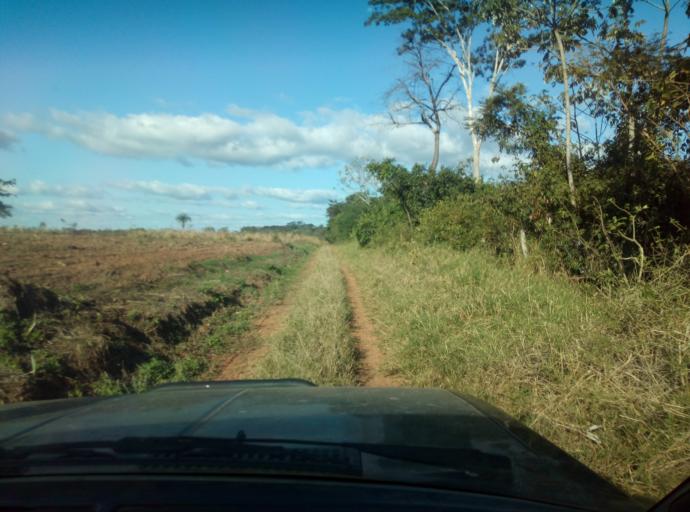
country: PY
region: Caaguazu
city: Carayao
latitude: -25.1734
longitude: -56.2795
